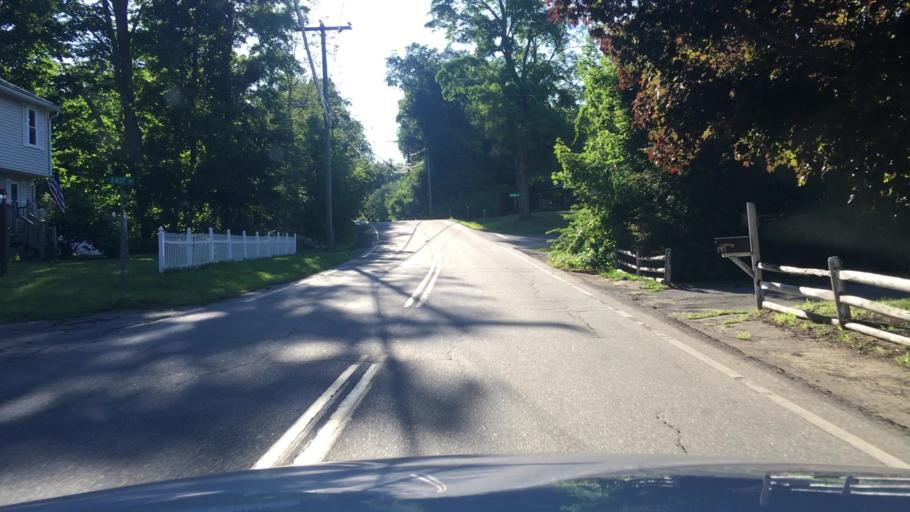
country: US
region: New Hampshire
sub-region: Rockingham County
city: Danville
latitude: 42.9057
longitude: -71.1533
